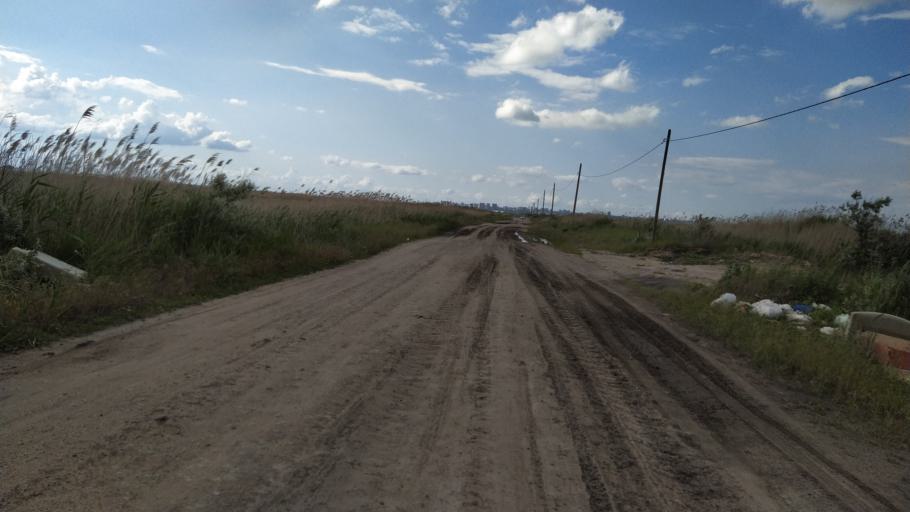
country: RU
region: Rostov
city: Bataysk
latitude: 47.1275
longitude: 39.6635
